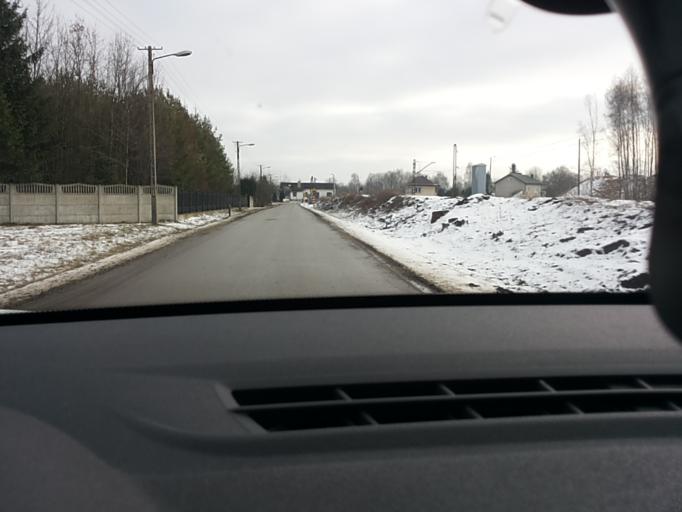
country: PL
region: Lodz Voivodeship
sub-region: Skierniewice
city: Skierniewice
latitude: 51.9668
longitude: 20.1229
